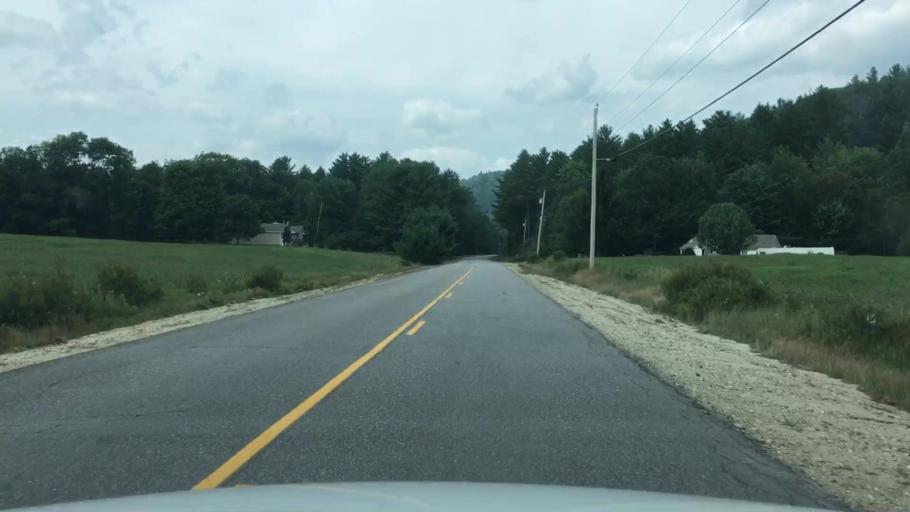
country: US
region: Maine
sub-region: Oxford County
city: Rumford
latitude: 44.5421
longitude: -70.6758
